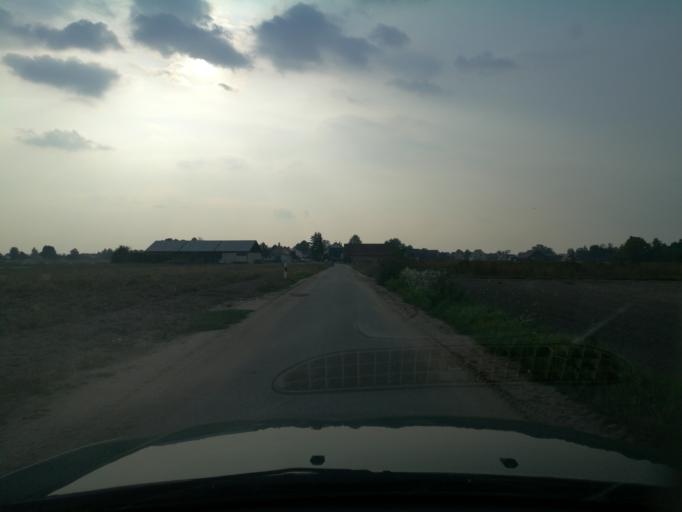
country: DE
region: Bavaria
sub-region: Regierungsbezirk Mittelfranken
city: Wetzendorf
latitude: 49.5197
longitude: 11.0598
